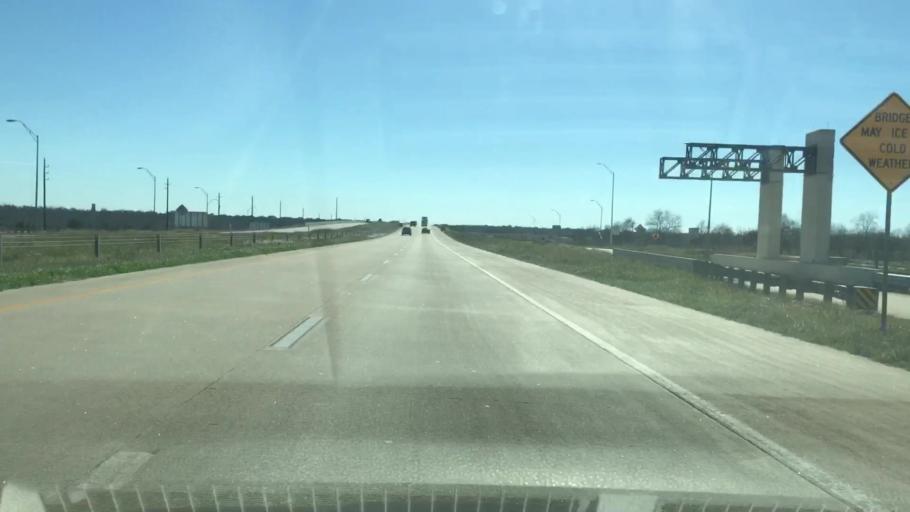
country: US
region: Texas
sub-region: Harris County
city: Cypress
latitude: 29.9821
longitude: -95.7697
